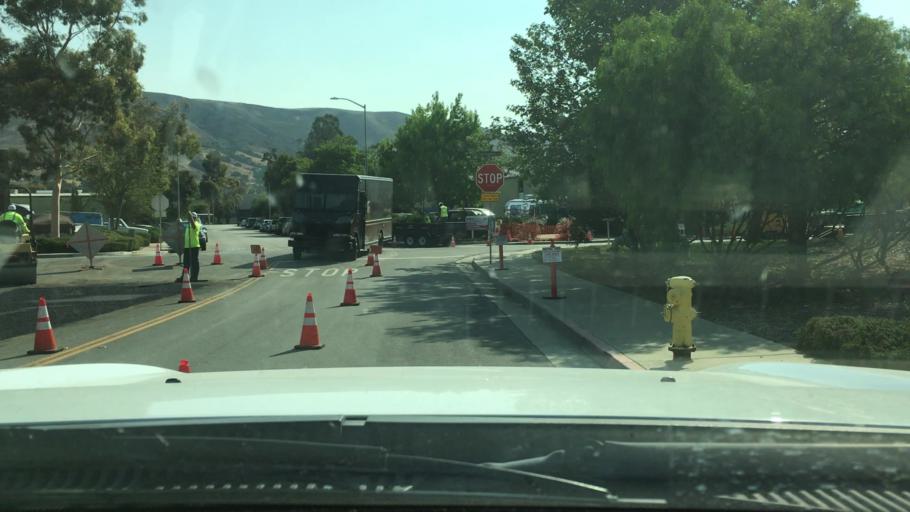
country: US
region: California
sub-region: San Luis Obispo County
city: San Luis Obispo
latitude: 35.2570
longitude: -120.6449
